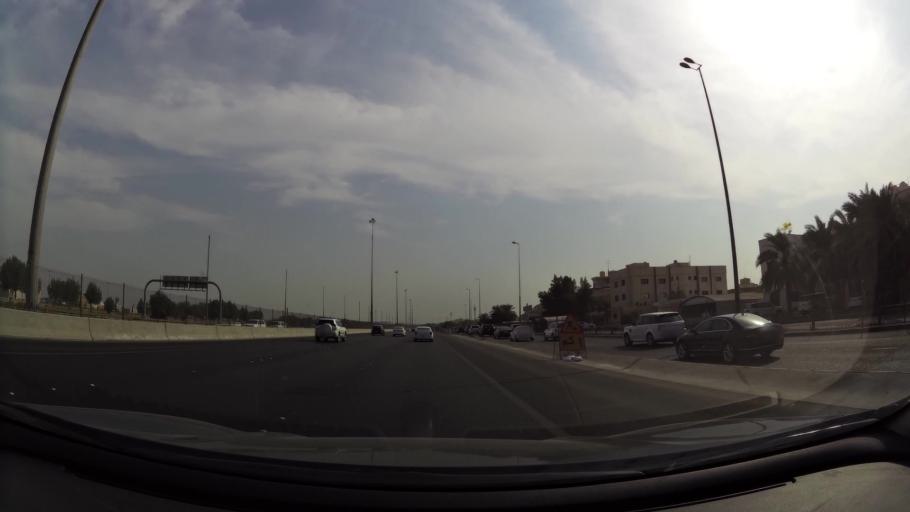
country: KW
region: Al Farwaniyah
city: Janub as Surrah
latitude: 29.2958
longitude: 47.9814
